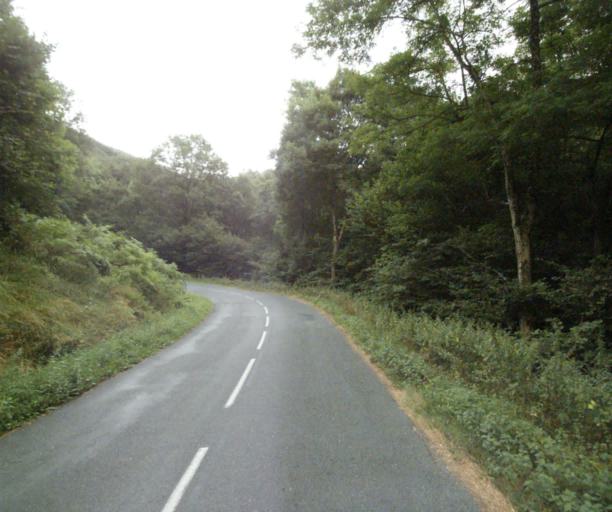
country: FR
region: Midi-Pyrenees
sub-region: Departement du Tarn
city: Soreze
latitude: 43.4354
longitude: 2.0848
